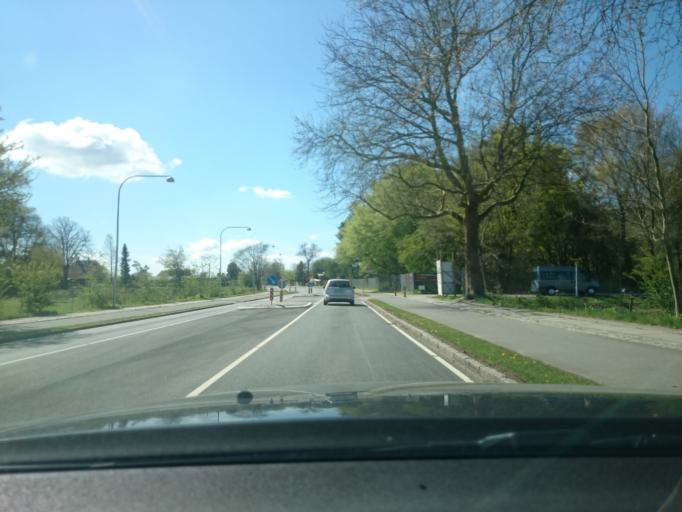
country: DK
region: Capital Region
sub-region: Lyngby-Tarbaek Kommune
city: Kongens Lyngby
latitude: 55.7787
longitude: 12.5379
